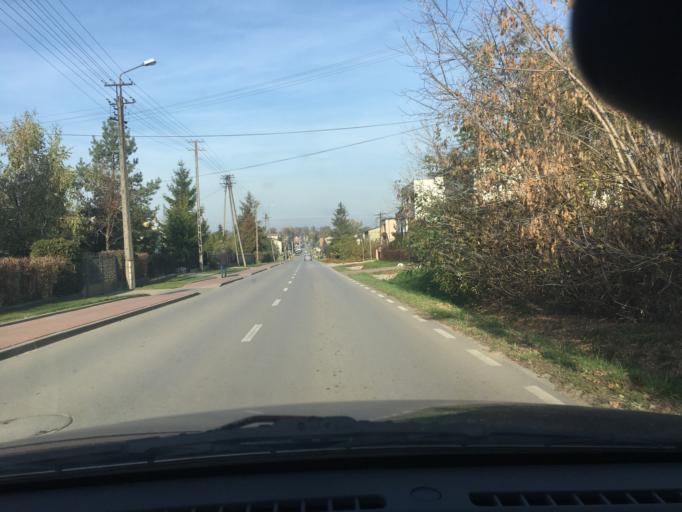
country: PL
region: Masovian Voivodeship
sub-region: Powiat plocki
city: Bodzanow
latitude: 52.4937
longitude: 20.0310
